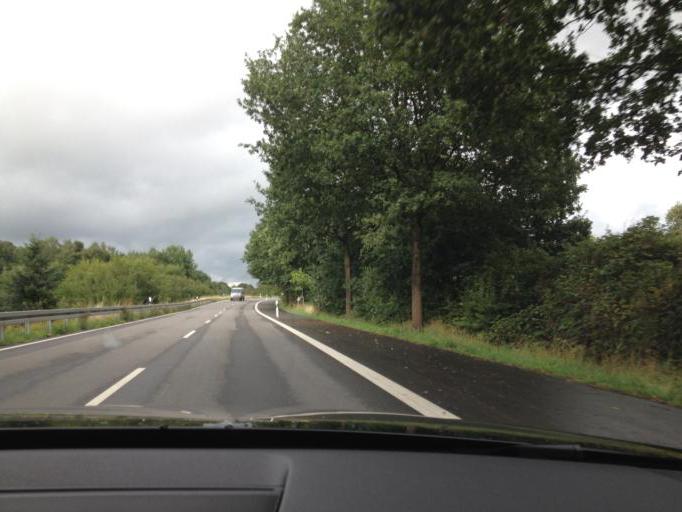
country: DE
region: Saarland
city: Oberthal
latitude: 49.5160
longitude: 7.0932
